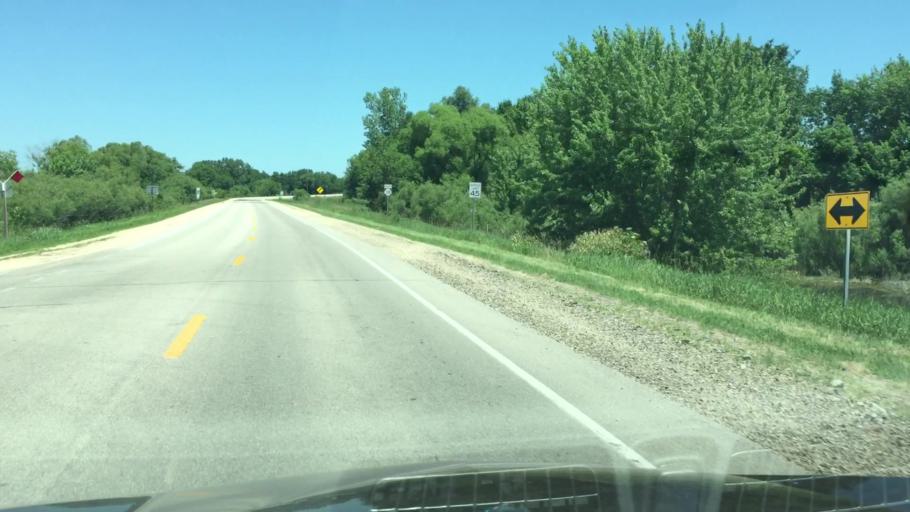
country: US
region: Iowa
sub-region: Cedar County
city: Mechanicsville
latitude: 42.0023
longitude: -91.1418
